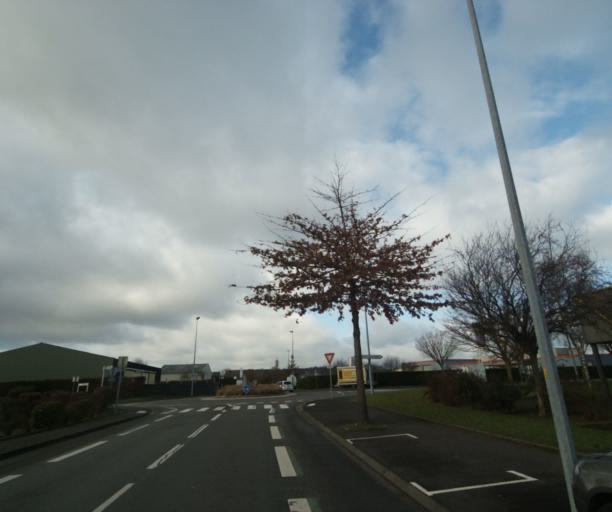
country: FR
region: Pays de la Loire
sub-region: Departement de la Sarthe
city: Rouillon
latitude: 48.0128
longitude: 0.1510
